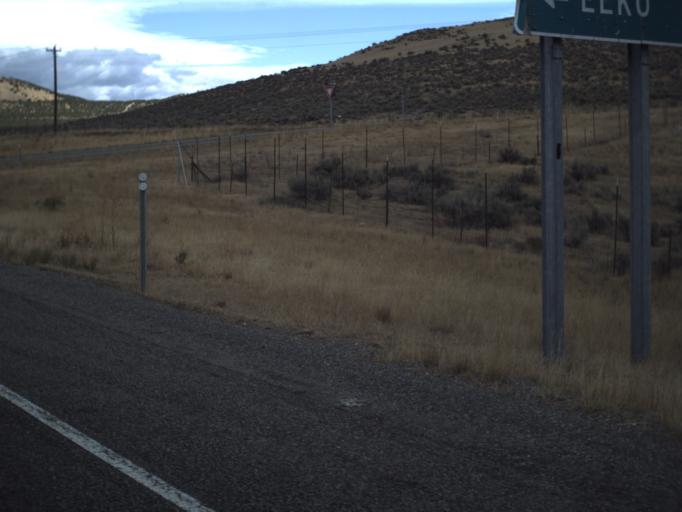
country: US
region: Idaho
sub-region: Oneida County
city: Malad City
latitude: 41.9645
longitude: -112.7536
